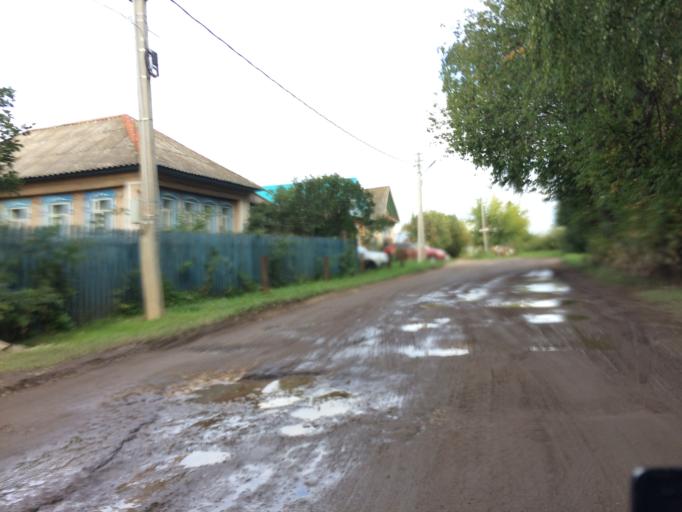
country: RU
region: Mariy-El
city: Yoshkar-Ola
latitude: 56.6544
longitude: 48.0120
